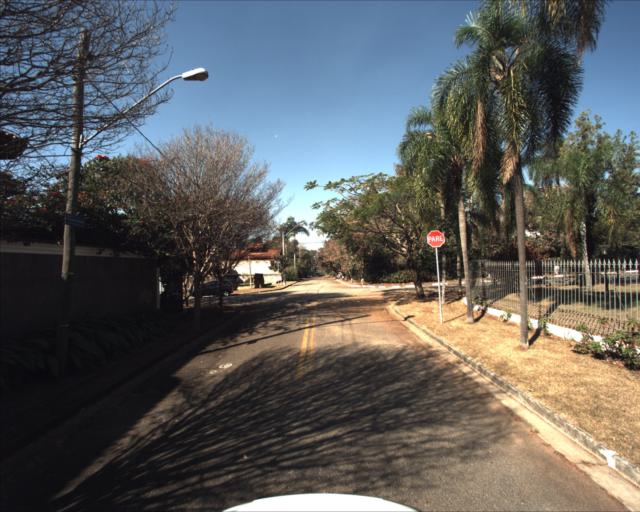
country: BR
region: Sao Paulo
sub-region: Sorocaba
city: Sorocaba
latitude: -23.4953
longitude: -47.4120
